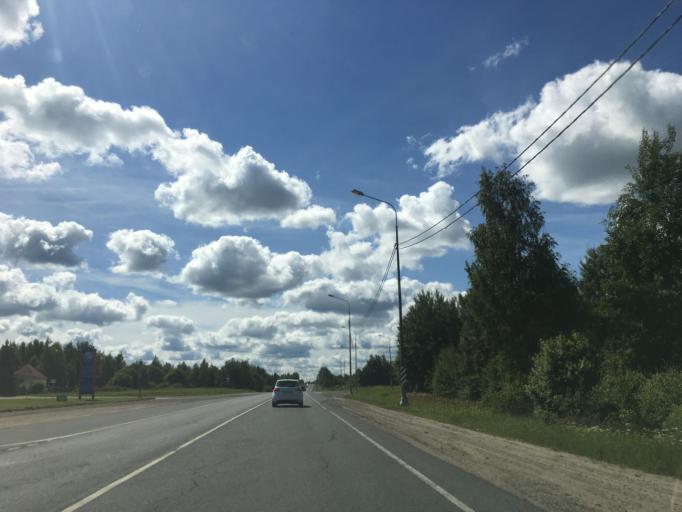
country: RU
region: Pskov
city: Ostrov
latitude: 57.3327
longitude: 28.3694
